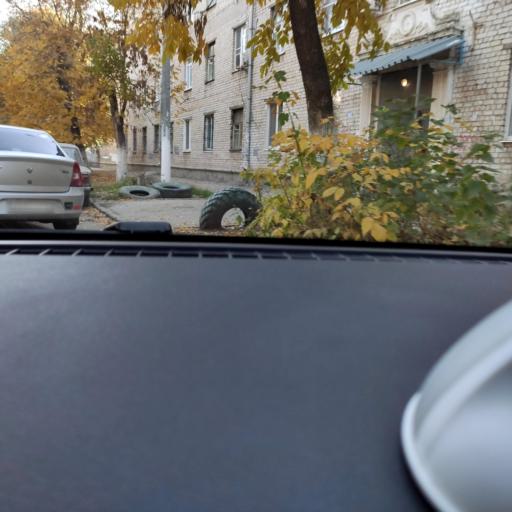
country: RU
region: Samara
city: Samara
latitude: 53.2224
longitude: 50.2637
